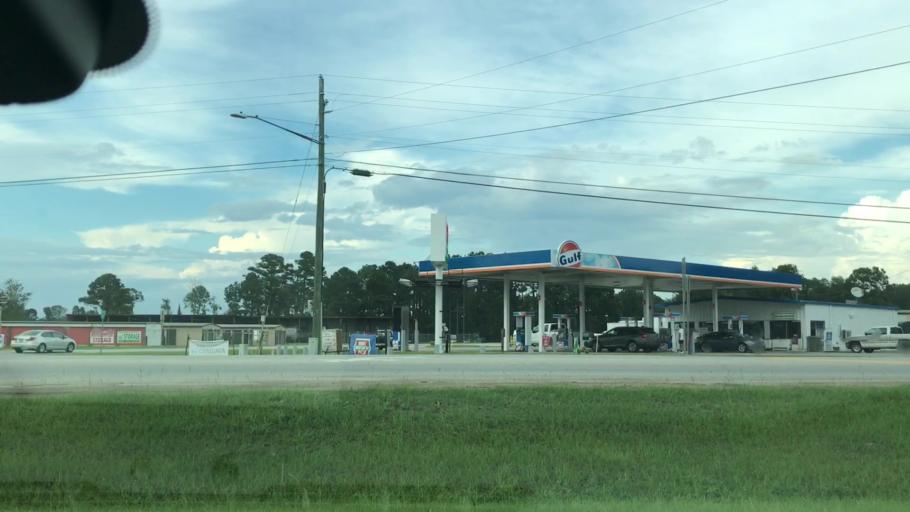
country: US
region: Georgia
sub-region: Quitman County
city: Georgetown
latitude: 31.8825
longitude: -85.0933
